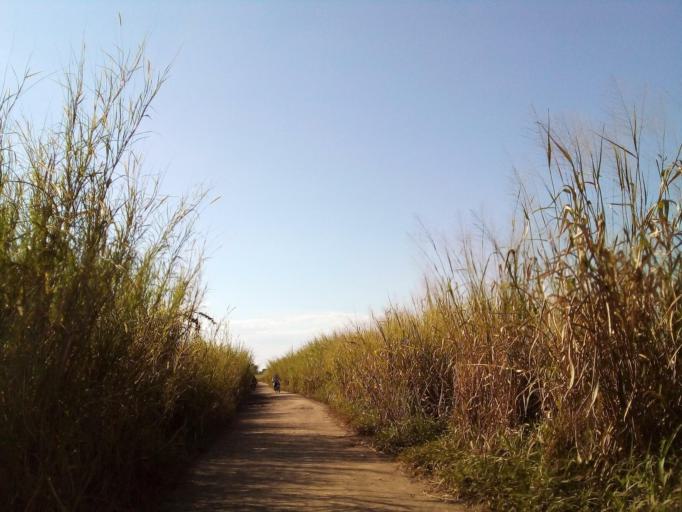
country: MZ
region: Zambezia
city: Quelimane
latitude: -17.5477
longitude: 36.6950
